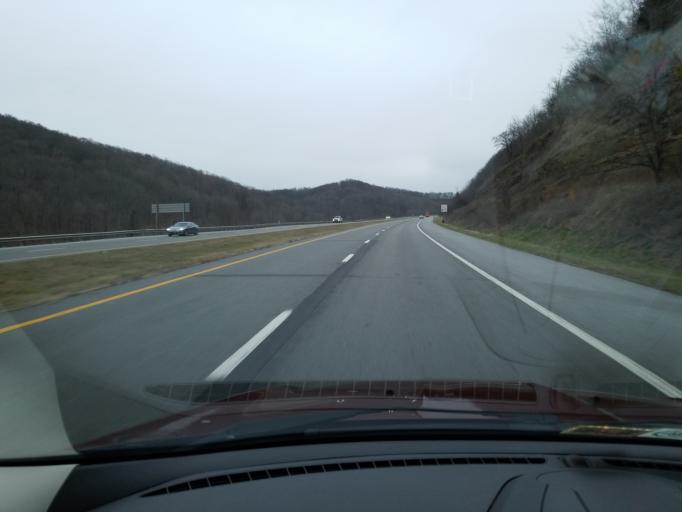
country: US
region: West Virginia
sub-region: Mercer County
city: Athens
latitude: 37.3413
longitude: -81.0025
